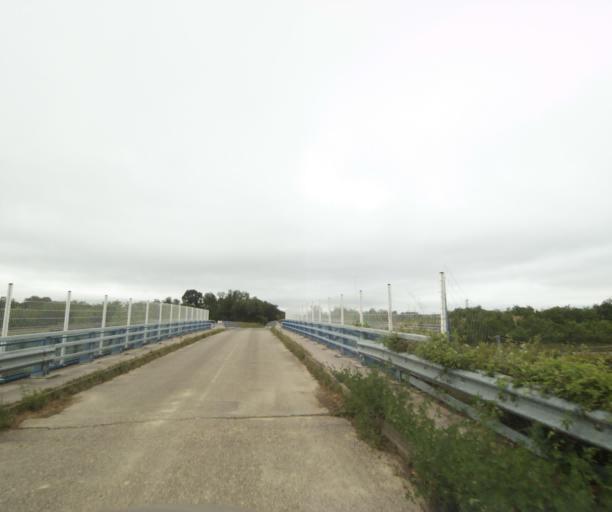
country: FR
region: Rhone-Alpes
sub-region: Departement de l'Ain
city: Tramoyes
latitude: 45.8577
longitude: 4.9464
